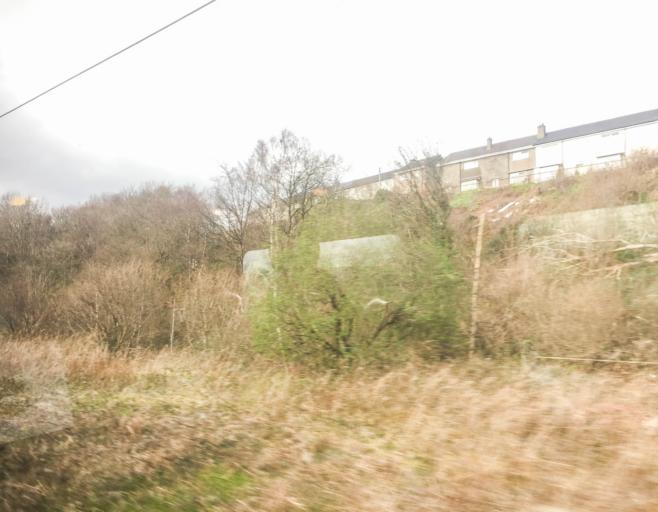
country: GB
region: Scotland
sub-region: West Dunbartonshire
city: Renton
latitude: 55.9471
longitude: -4.6025
